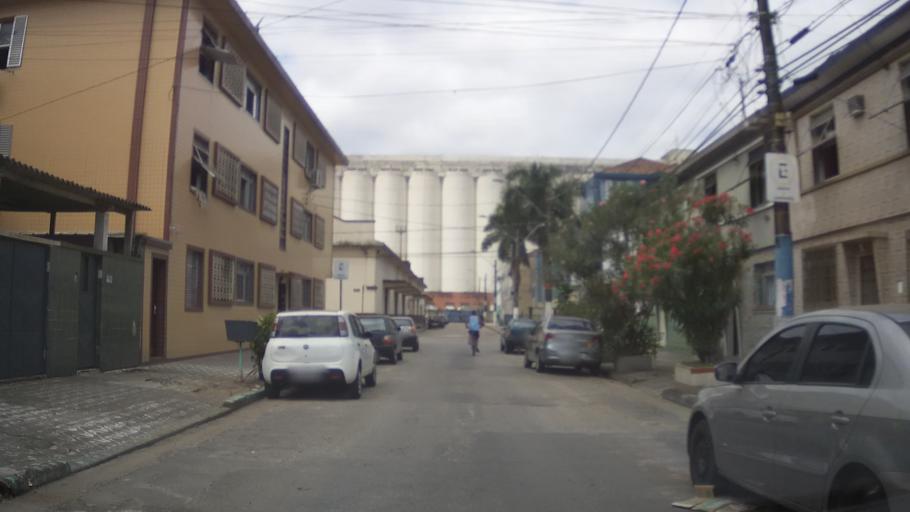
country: BR
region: Sao Paulo
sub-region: Santos
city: Santos
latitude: -23.9589
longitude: -46.3105
